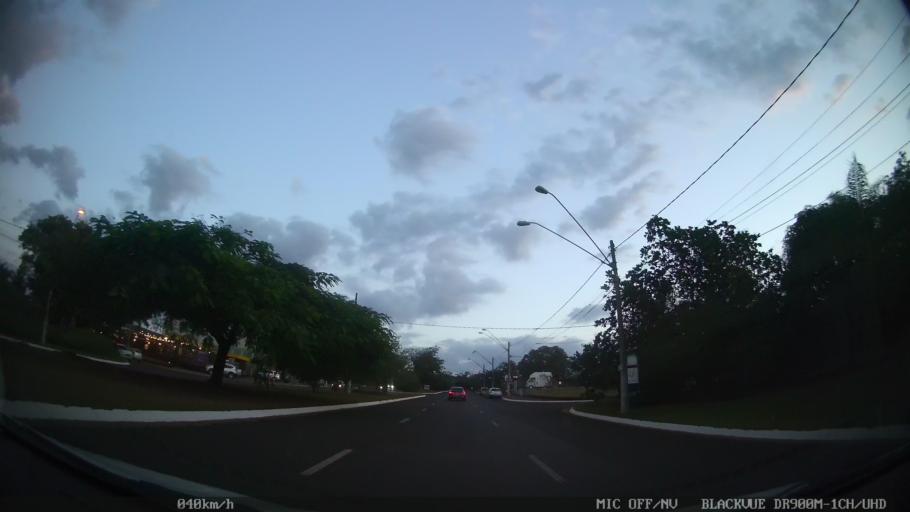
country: BR
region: Sao Paulo
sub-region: Ribeirao Preto
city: Ribeirao Preto
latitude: -21.2139
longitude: -47.7796
